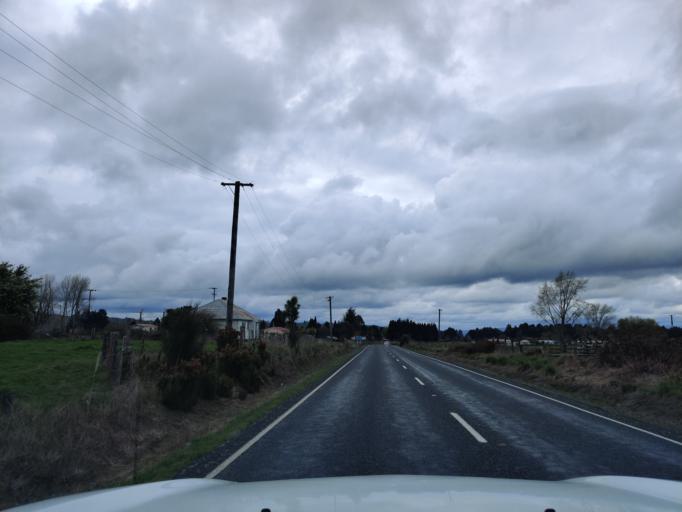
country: NZ
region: Waikato
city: Turangi
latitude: -39.0062
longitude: 175.3770
